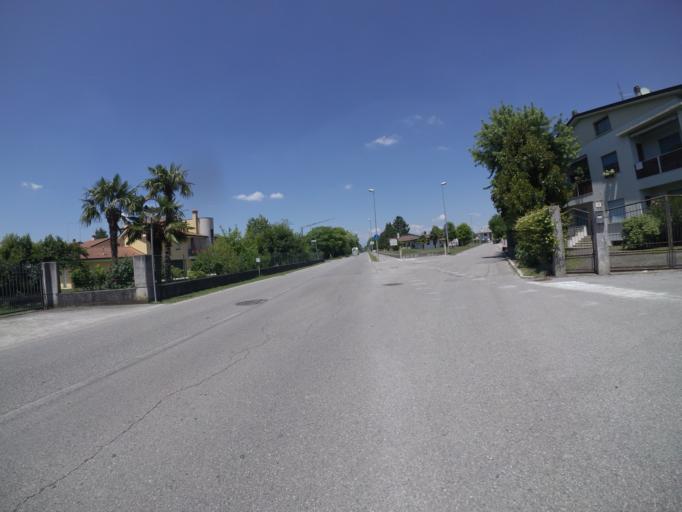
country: IT
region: Friuli Venezia Giulia
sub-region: Provincia di Udine
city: Rivignano
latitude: 45.8795
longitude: 13.0397
